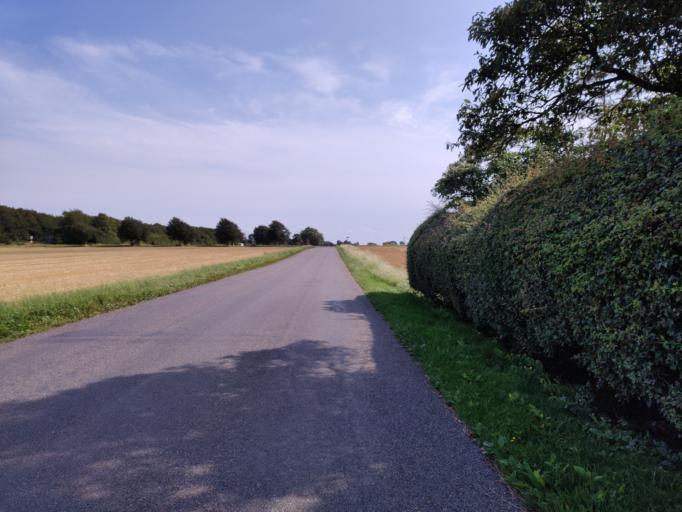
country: DK
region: Zealand
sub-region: Guldborgsund Kommune
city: Nykobing Falster
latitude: 54.6211
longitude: 11.9123
